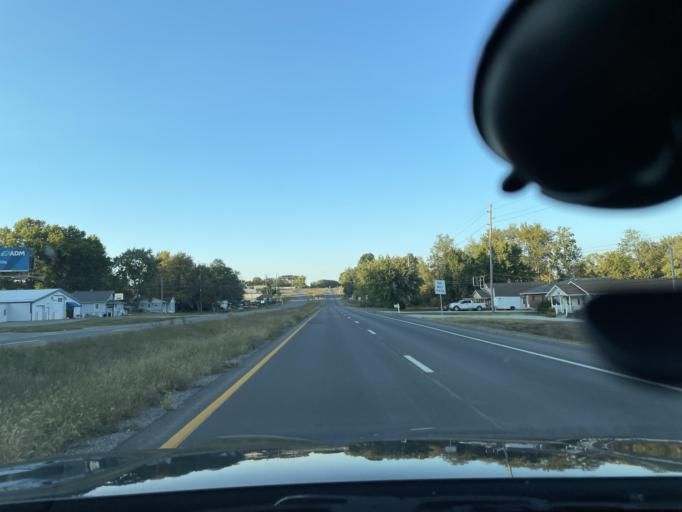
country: US
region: Missouri
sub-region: Andrew County
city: Country Club Village
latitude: 39.8107
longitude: -94.8407
